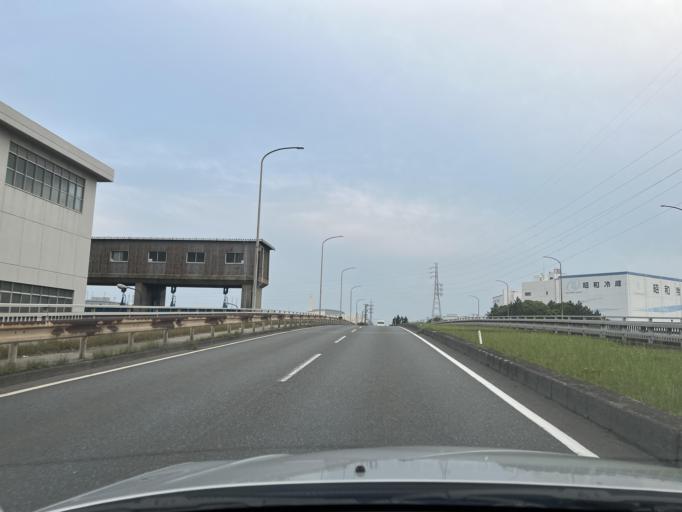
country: JP
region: Chiba
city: Funabashi
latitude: 35.6819
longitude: 139.9629
